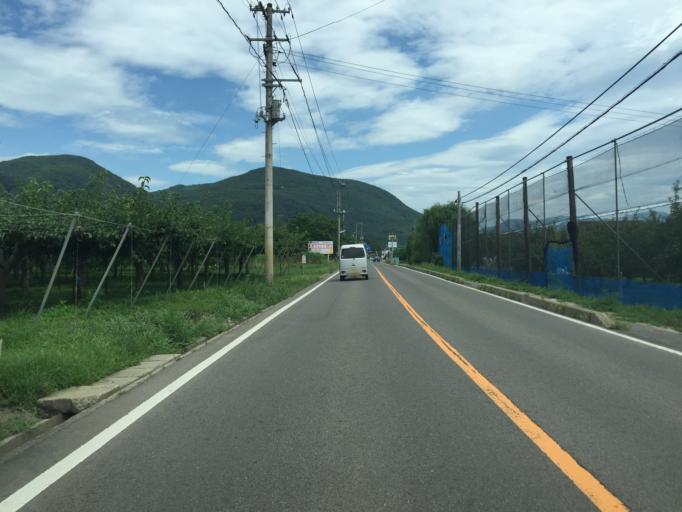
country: JP
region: Fukushima
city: Fukushima-shi
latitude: 37.7950
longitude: 140.4007
